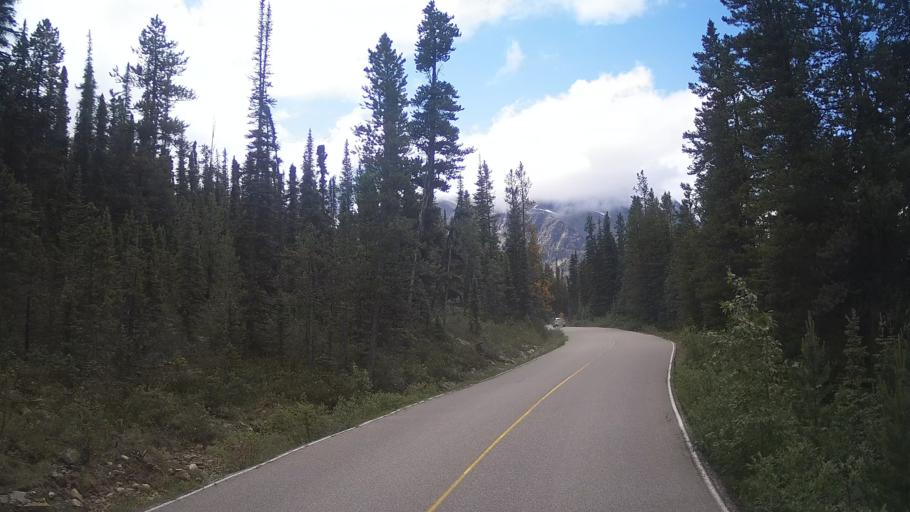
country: CA
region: Alberta
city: Jasper Park Lodge
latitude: 52.7205
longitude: -118.0519
